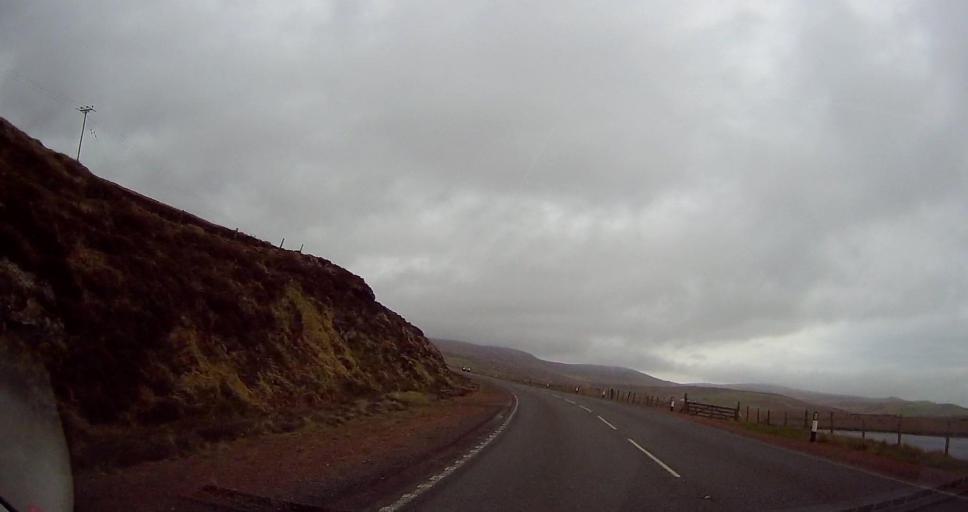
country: GB
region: Scotland
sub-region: Shetland Islands
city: Lerwick
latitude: 60.2589
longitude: -1.2228
